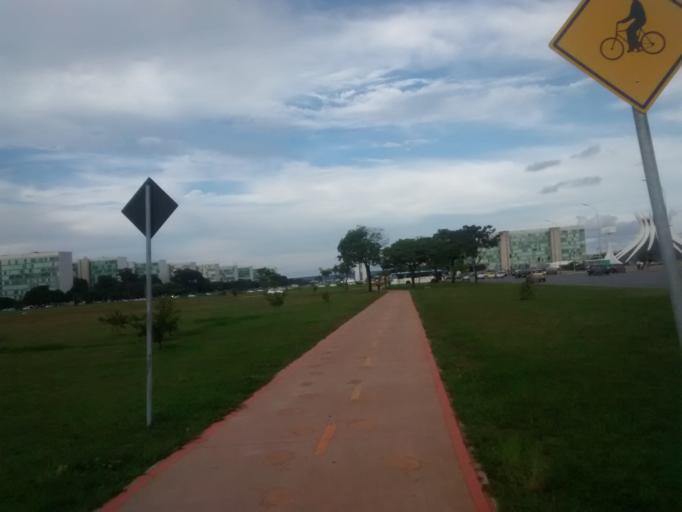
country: BR
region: Federal District
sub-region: Brasilia
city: Brasilia
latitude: -15.7960
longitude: -47.8786
